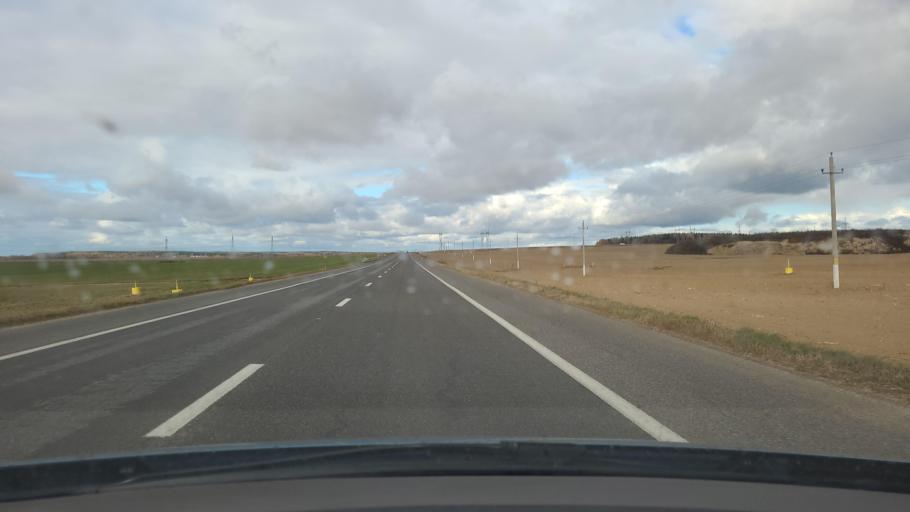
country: BY
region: Grodnenskaya
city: Astravyets
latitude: 54.7478
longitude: 26.0799
